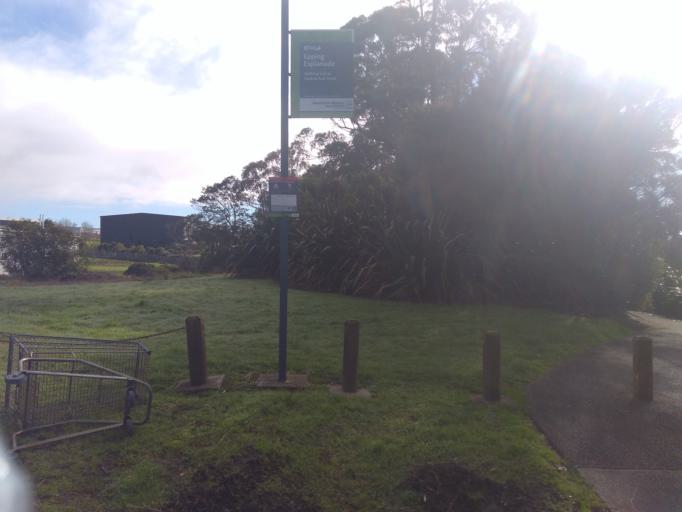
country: NZ
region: Auckland
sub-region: Auckland
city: Rosebank
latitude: -36.8671
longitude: 174.6353
